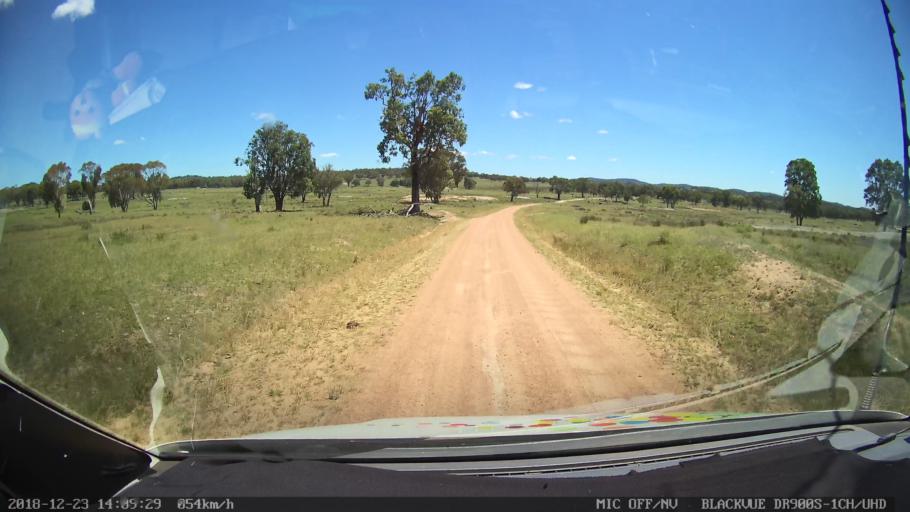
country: AU
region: New South Wales
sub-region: Tamworth Municipality
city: Manilla
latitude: -30.6455
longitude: 151.0619
